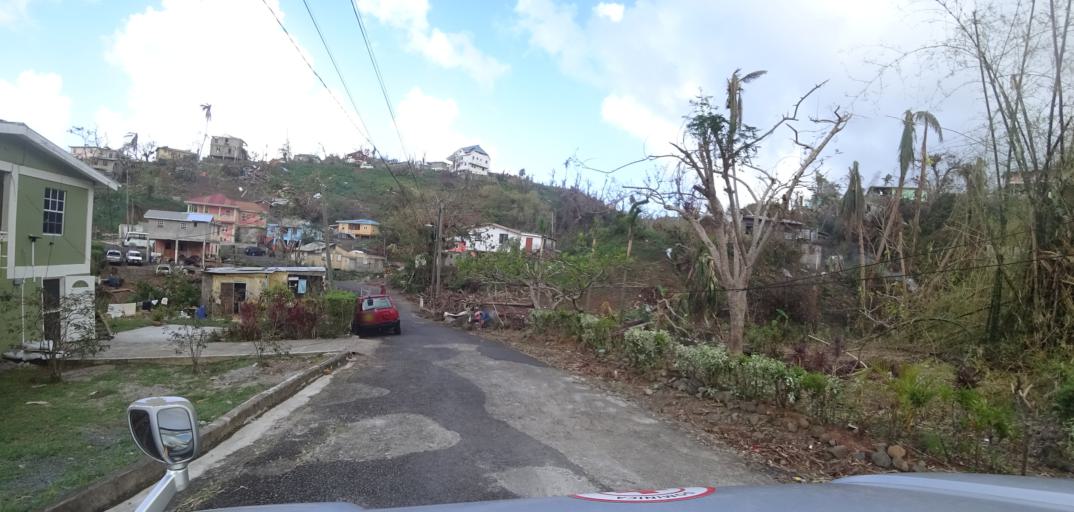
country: DM
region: Saint Andrew
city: Marigot
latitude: 15.5382
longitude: -61.2852
